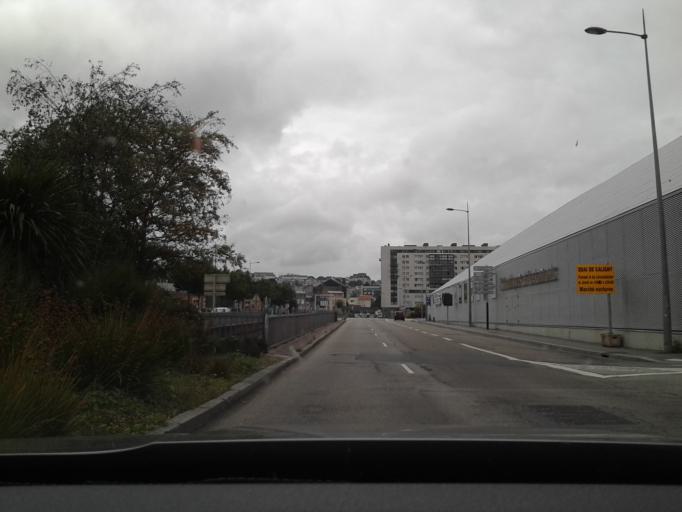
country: FR
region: Lower Normandy
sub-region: Departement de la Manche
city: Cherbourg-Octeville
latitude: 49.6338
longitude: -1.6178
